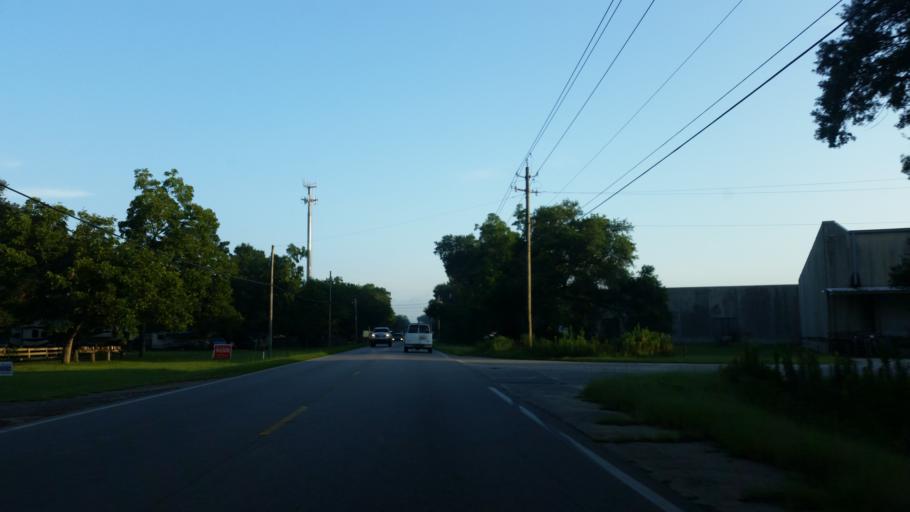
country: US
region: Florida
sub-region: Escambia County
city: Ensley
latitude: 30.5422
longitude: -87.2784
